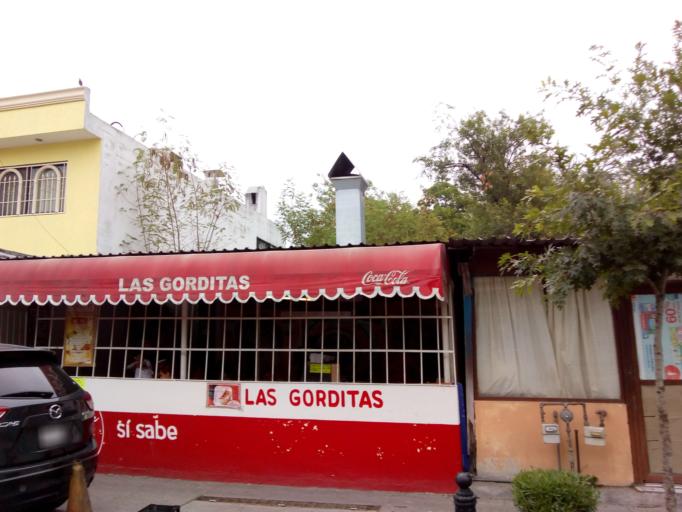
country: MX
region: Nuevo Leon
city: Guadalupe
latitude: 25.6791
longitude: -100.2598
